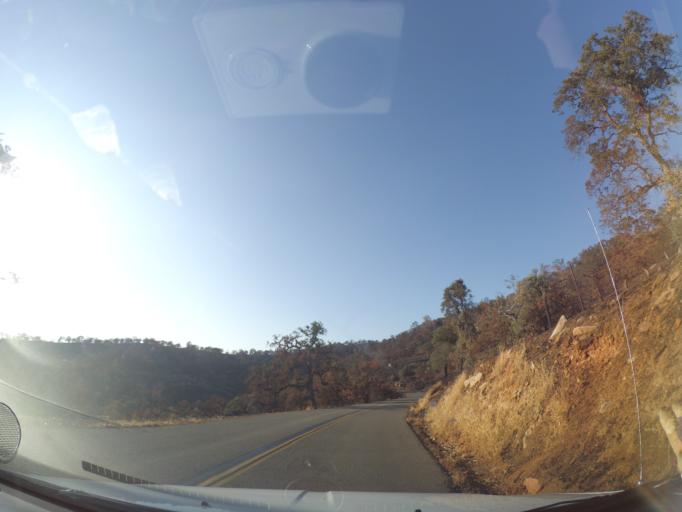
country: US
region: California
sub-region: Mariposa County
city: Mariposa
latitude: 37.5035
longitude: -120.1146
